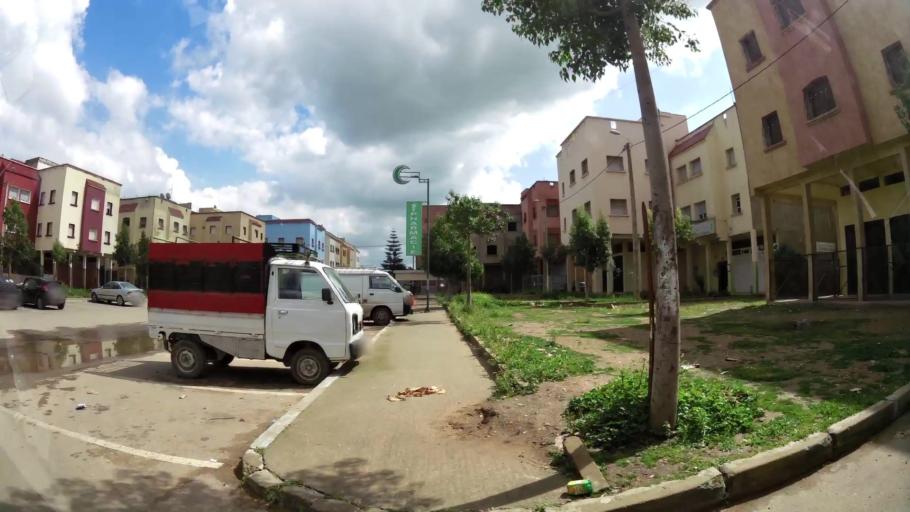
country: MA
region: Grand Casablanca
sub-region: Mediouna
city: Mediouna
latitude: 33.3668
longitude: -7.5292
